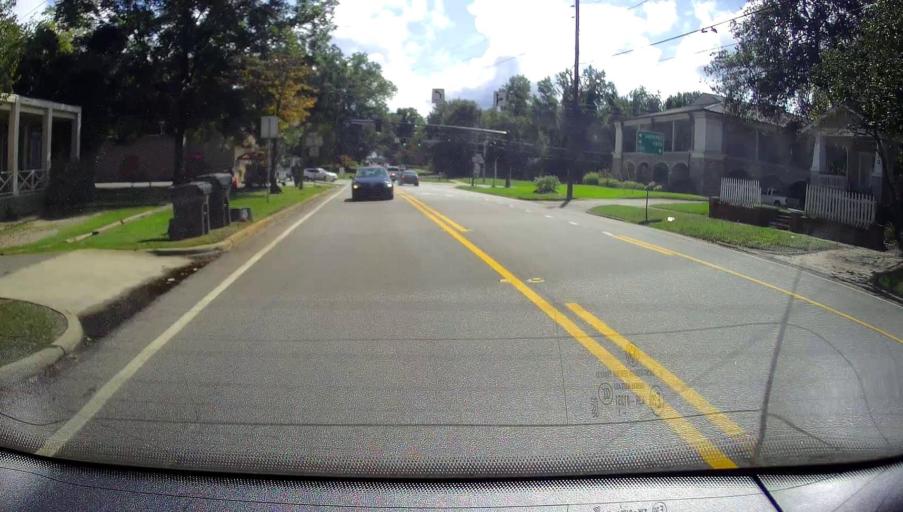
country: US
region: Georgia
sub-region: Baldwin County
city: Milledgeville
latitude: 33.0834
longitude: -83.2347
